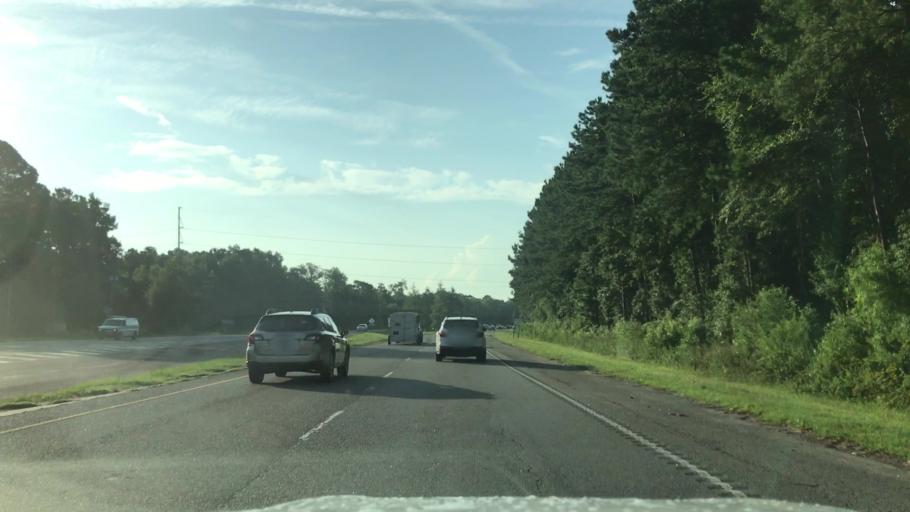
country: US
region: South Carolina
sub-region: Charleston County
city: Shell Point
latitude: 32.8191
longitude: -80.0672
